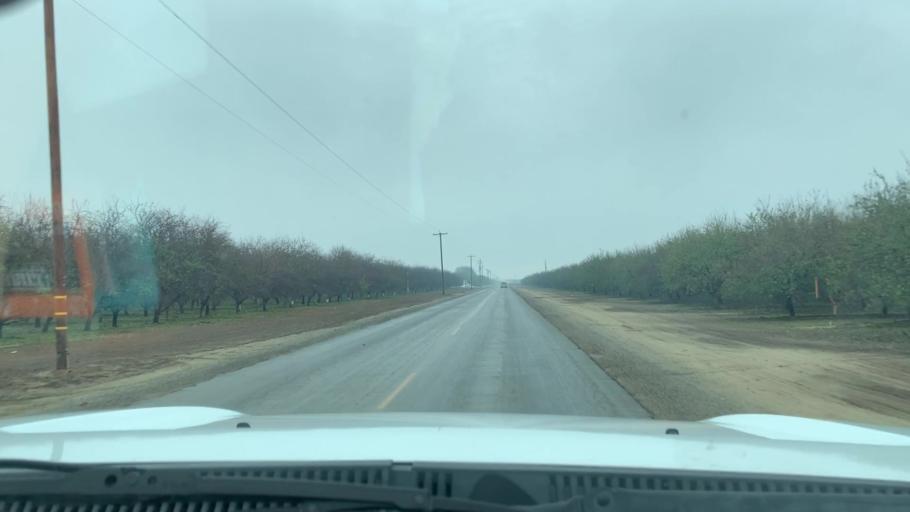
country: US
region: California
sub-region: Kern County
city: Delano
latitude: 35.7612
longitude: -119.3605
